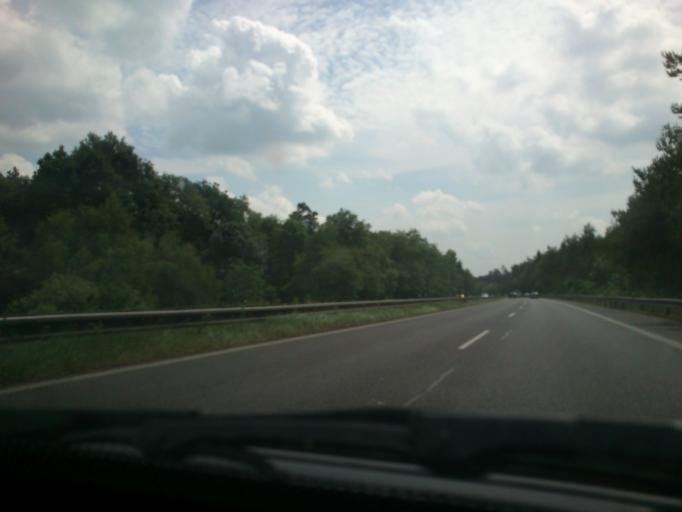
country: CZ
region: Central Bohemia
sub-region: Okres Mlada Boleslav
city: Mlada Boleslav
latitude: 50.3558
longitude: 14.8723
